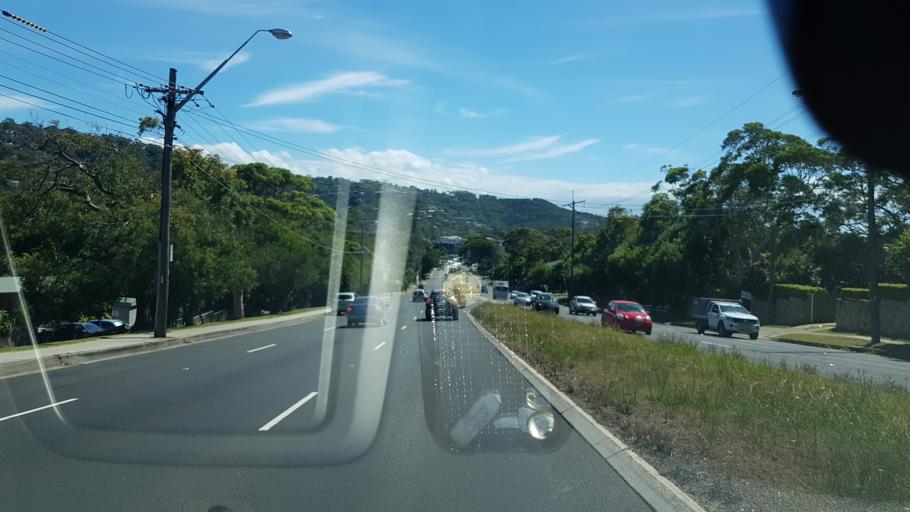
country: AU
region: New South Wales
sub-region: Pittwater
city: Newport
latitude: -33.6624
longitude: 151.3160
